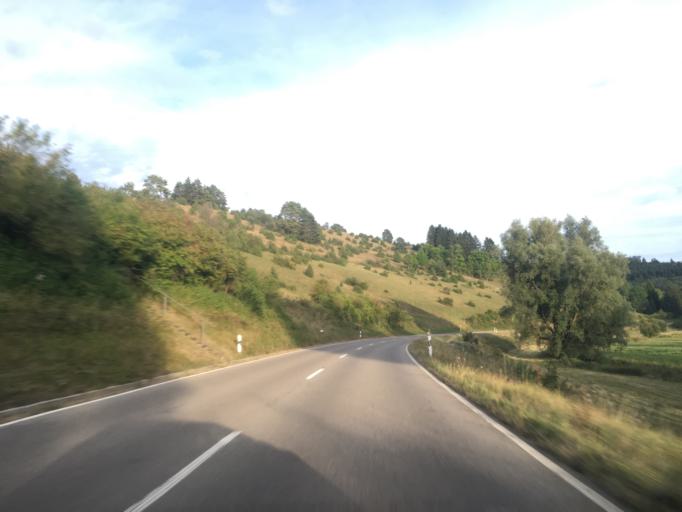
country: DE
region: Baden-Wuerttemberg
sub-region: Tuebingen Region
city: Gomadingen
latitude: 48.3981
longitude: 9.3967
